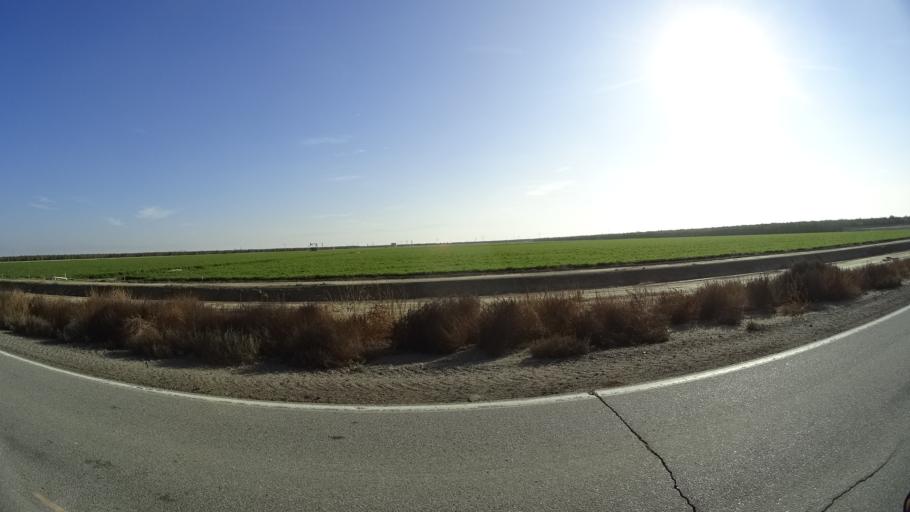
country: US
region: California
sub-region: Kern County
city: Rosedale
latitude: 35.2962
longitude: -119.1443
